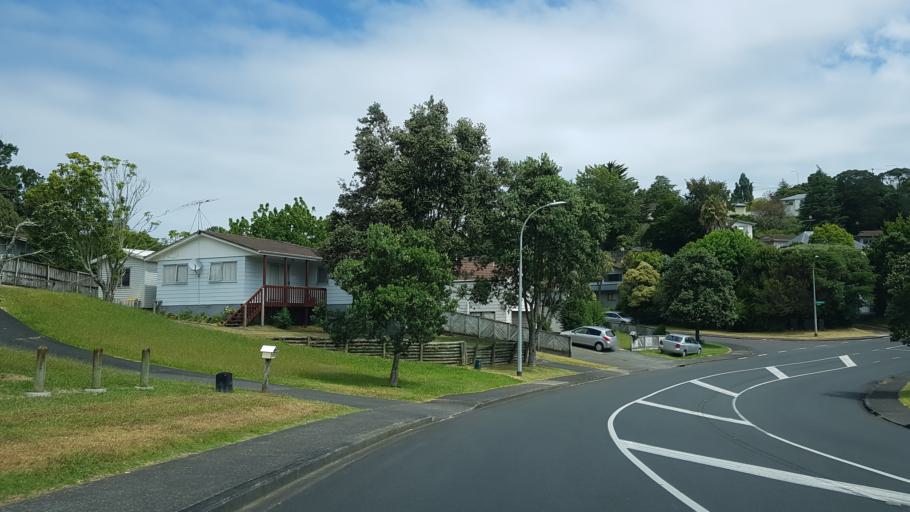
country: NZ
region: Auckland
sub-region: Auckland
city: North Shore
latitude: -36.7722
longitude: 174.7158
